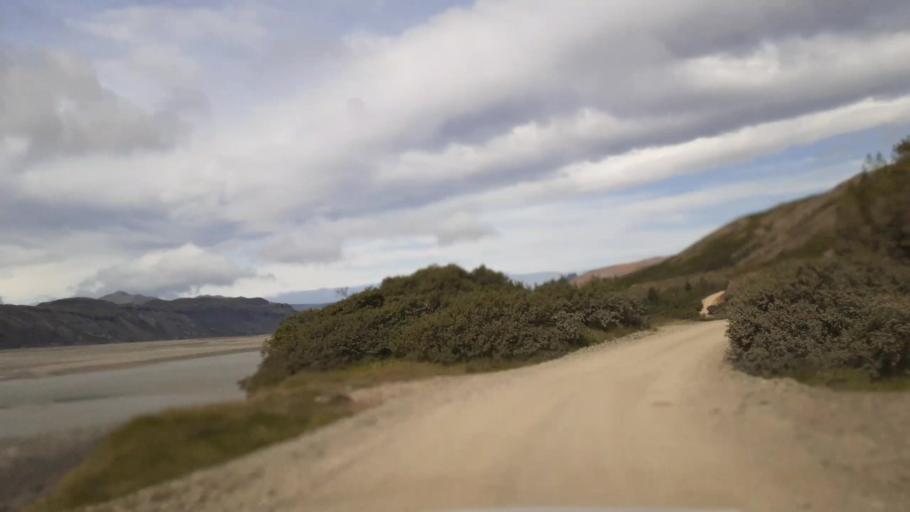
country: IS
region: East
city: Hoefn
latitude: 64.4358
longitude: -14.9069
